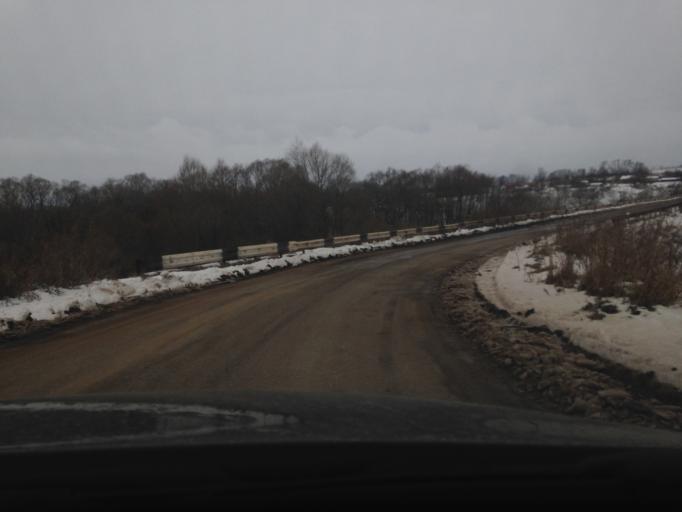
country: RU
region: Tula
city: Teploye
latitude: 53.7724
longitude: 37.6450
